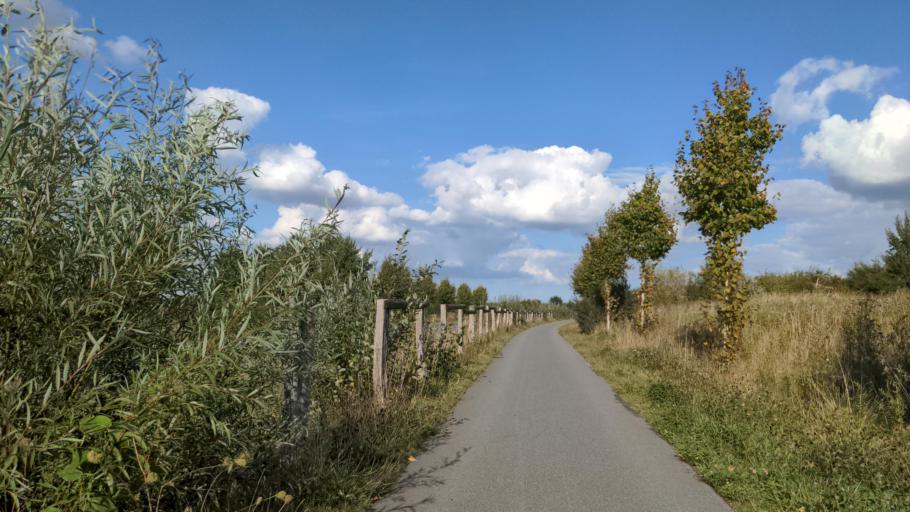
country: DE
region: Schleswig-Holstein
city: Stockelsdorf
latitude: 53.8867
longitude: 10.6056
